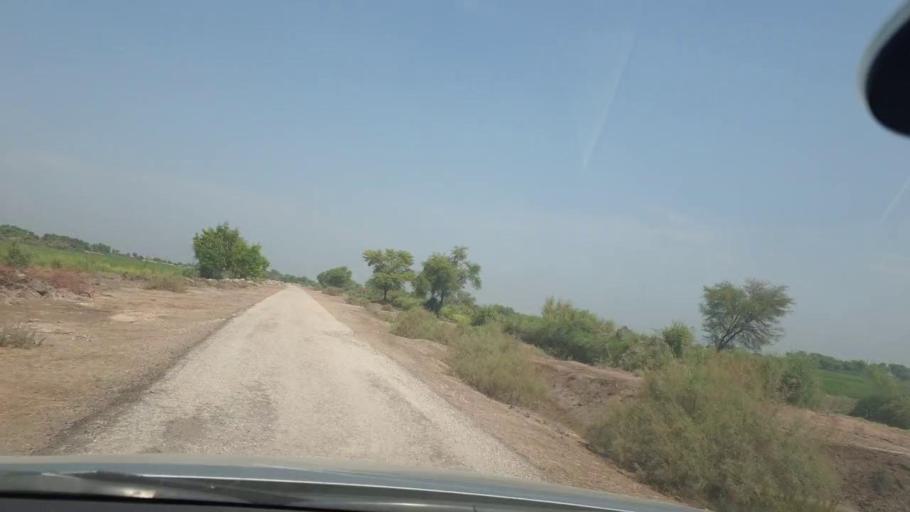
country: PK
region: Balochistan
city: Mehrabpur
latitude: 28.0820
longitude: 68.0419
